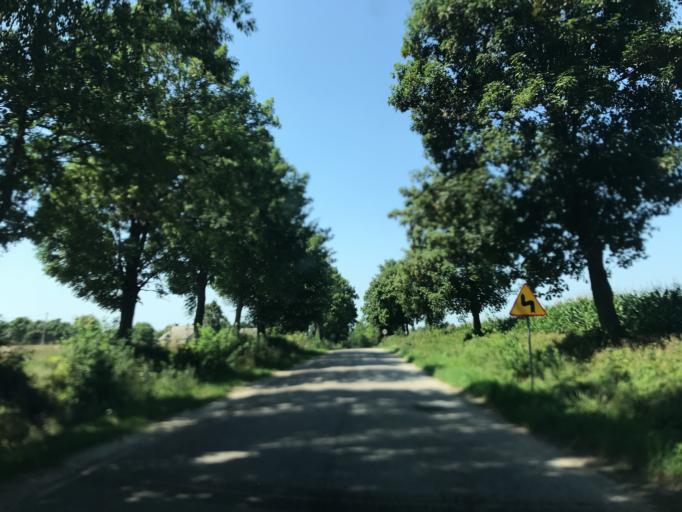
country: PL
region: Kujawsko-Pomorskie
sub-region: Powiat lipnowski
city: Chrostkowo
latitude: 52.9868
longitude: 19.2664
